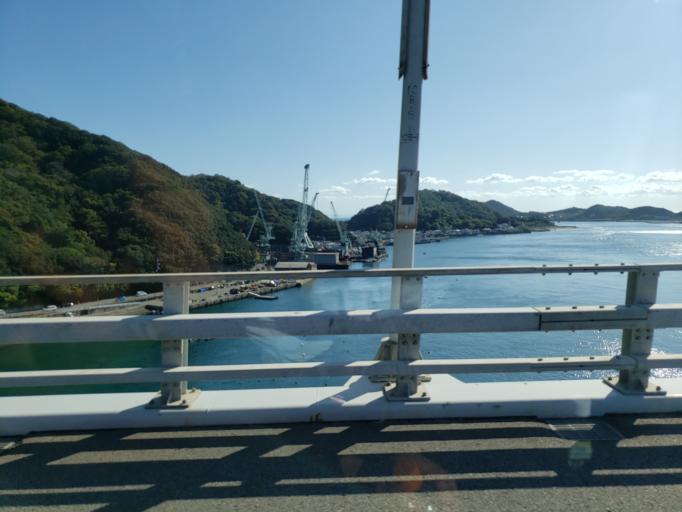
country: JP
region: Tokushima
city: Narutocho-mitsuishi
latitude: 34.1938
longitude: 134.6136
